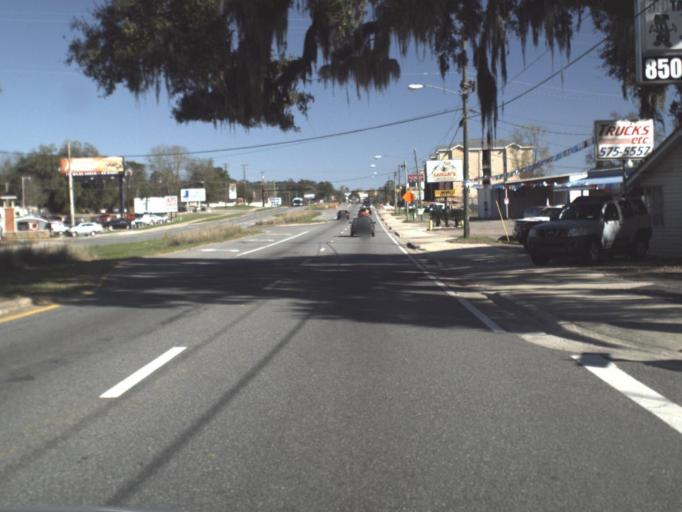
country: US
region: Florida
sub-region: Leon County
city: Tallahassee
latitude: 30.4516
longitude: -84.3356
